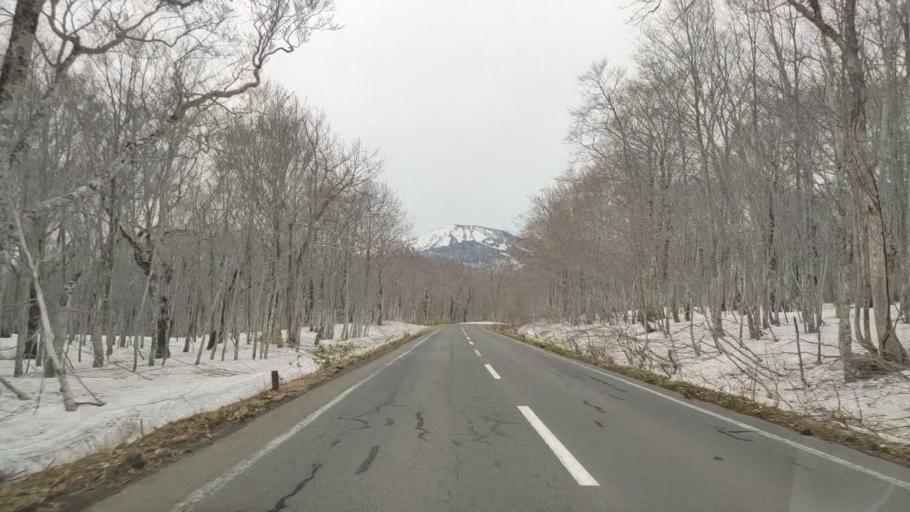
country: JP
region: Aomori
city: Aomori Shi
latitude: 40.6354
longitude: 140.9300
